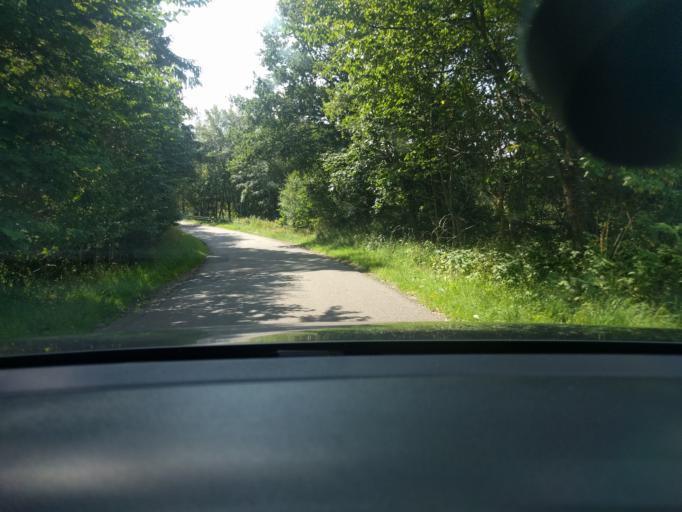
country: DK
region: Central Jutland
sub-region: Viborg Kommune
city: Bjerringbro
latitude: 56.5033
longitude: 9.5833
